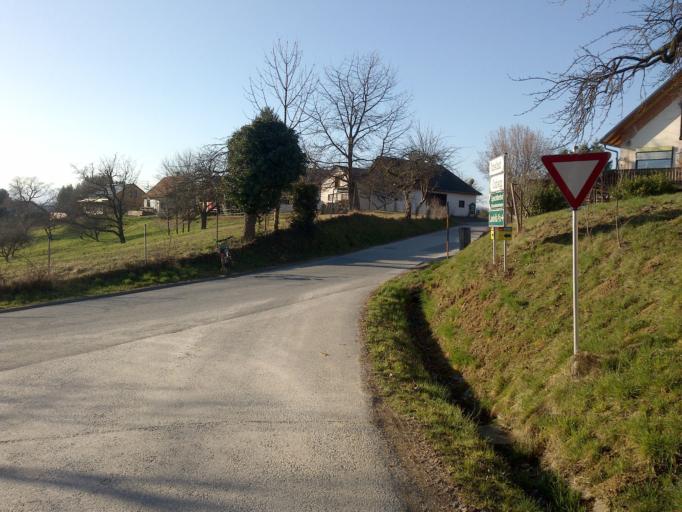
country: AT
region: Styria
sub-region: Politischer Bezirk Graz-Umgebung
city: Attendorf
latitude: 47.0098
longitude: 15.3406
